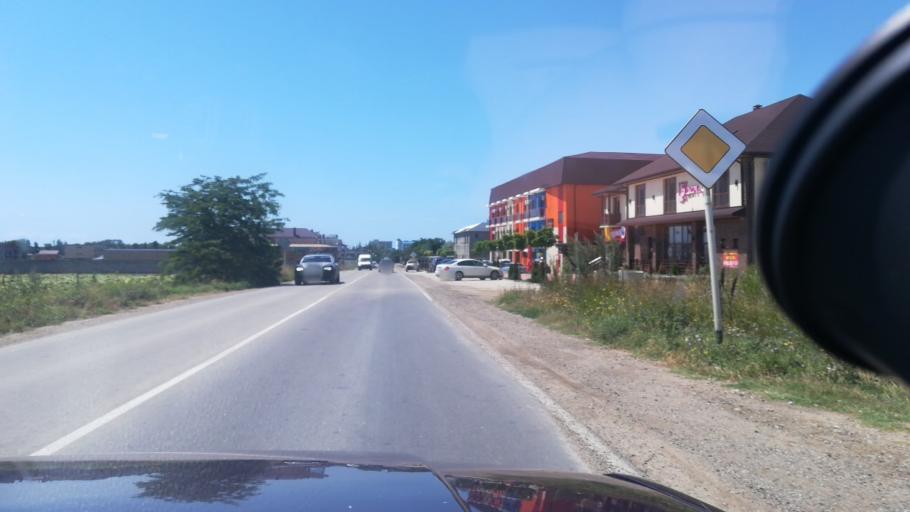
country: RU
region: Krasnodarskiy
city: Vityazevo
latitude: 44.9615
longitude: 37.3020
